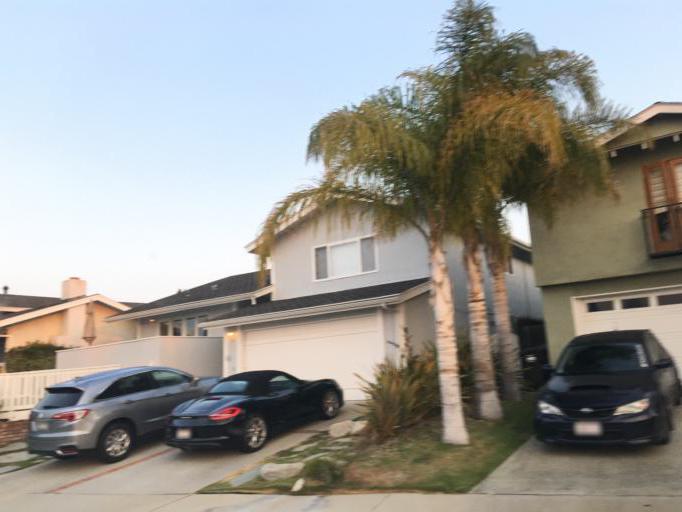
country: US
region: California
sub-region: Los Angeles County
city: Topanga
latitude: 34.0435
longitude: -118.5759
